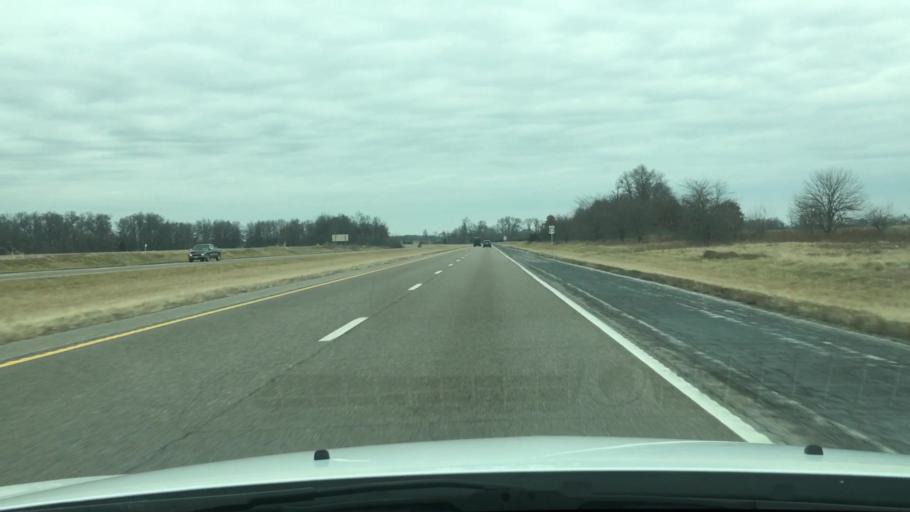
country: US
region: Missouri
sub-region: Audrain County
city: Mexico
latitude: 39.0236
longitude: -91.8856
